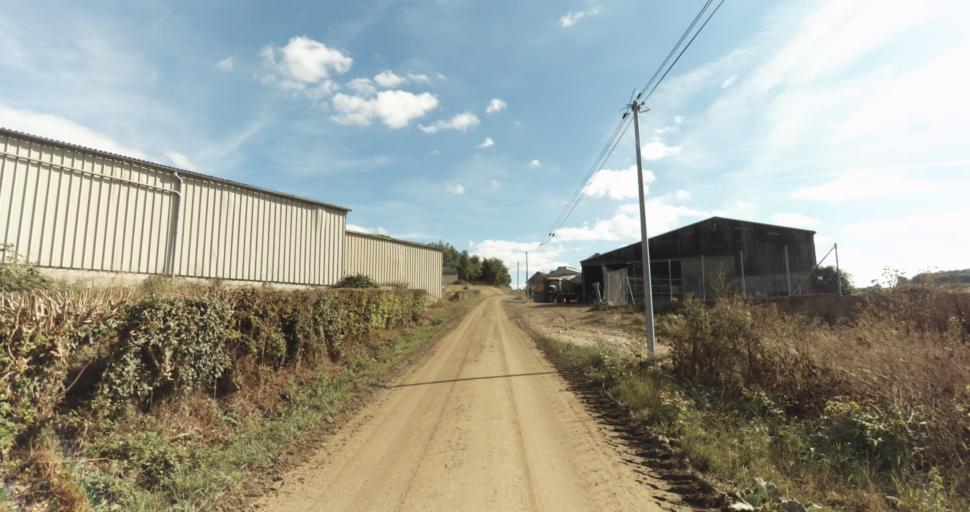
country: FR
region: Lower Normandy
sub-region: Departement de l'Orne
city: Vimoutiers
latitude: 48.9321
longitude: 0.1305
